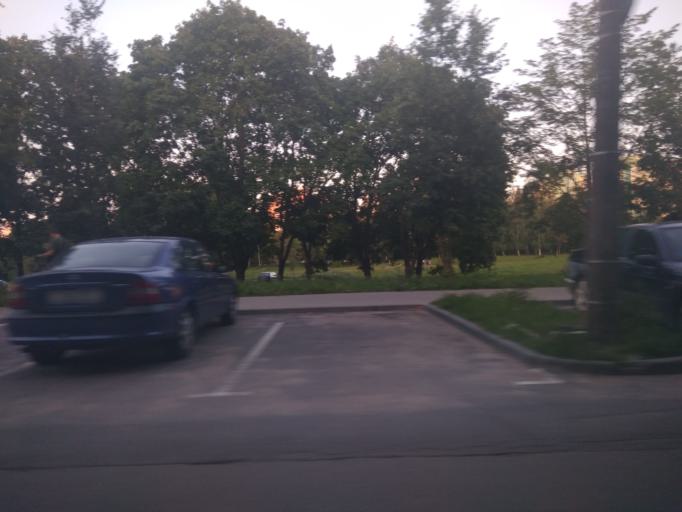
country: BY
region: Minsk
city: Novoye Medvezhino
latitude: 53.9277
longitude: 27.4771
